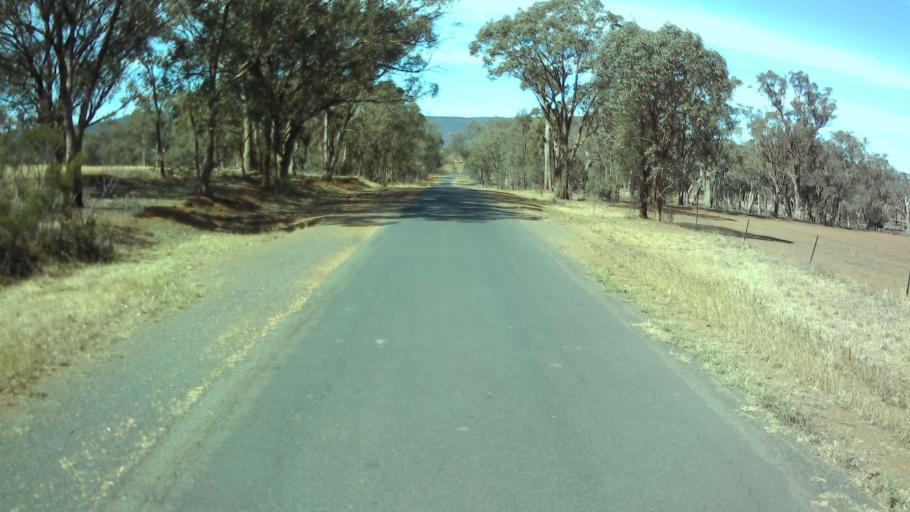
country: AU
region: New South Wales
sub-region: Weddin
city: Grenfell
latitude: -33.9365
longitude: 148.0814
